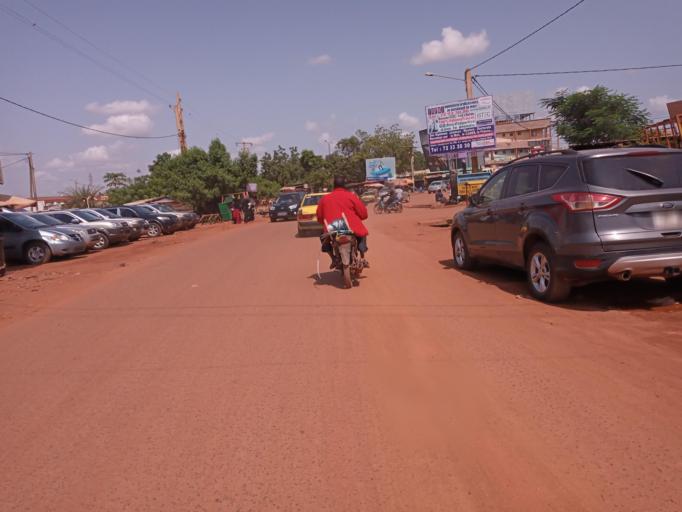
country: ML
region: Bamako
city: Bamako
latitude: 12.5963
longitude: -8.0170
